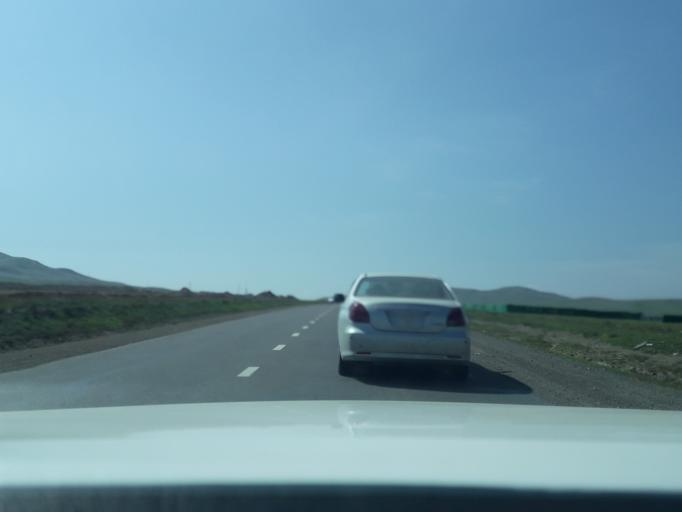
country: MN
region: Ulaanbaatar
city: Ulaanbaatar
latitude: 47.8143
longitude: 106.7548
